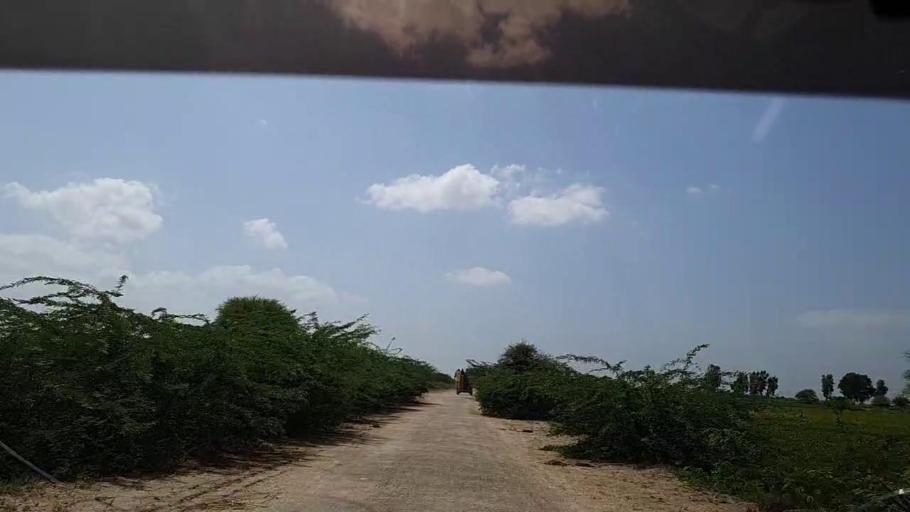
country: PK
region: Sindh
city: Badin
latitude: 24.5624
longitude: 68.7490
